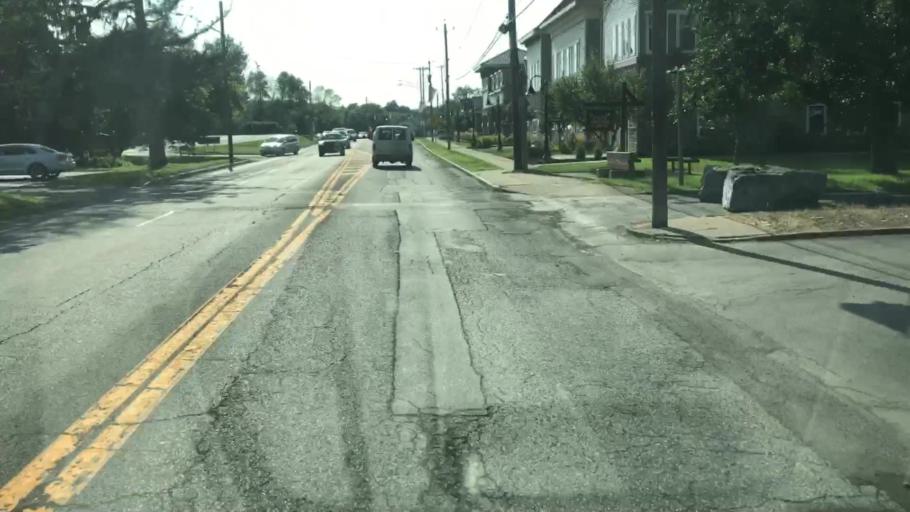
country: US
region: New York
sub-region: Onondaga County
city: Manlius
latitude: 43.0069
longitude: -75.9867
